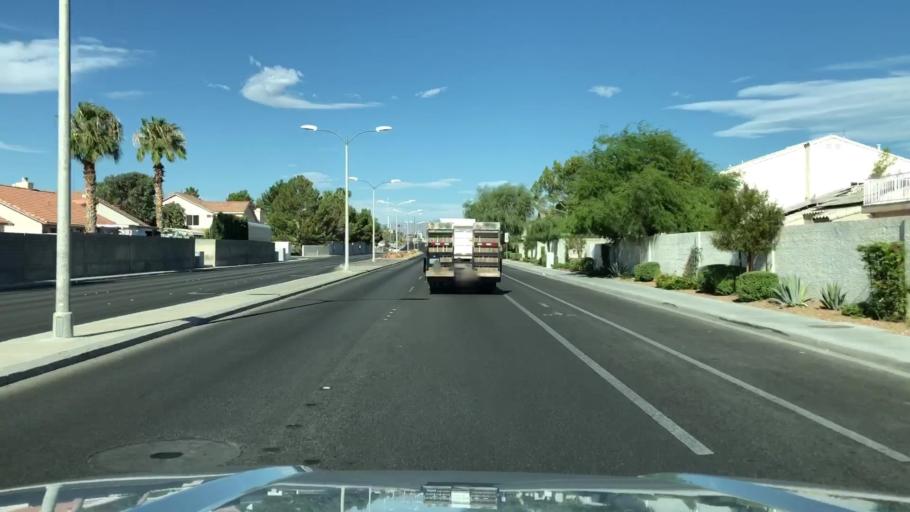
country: US
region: Nevada
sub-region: Clark County
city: Whitney
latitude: 36.0424
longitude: -115.1126
